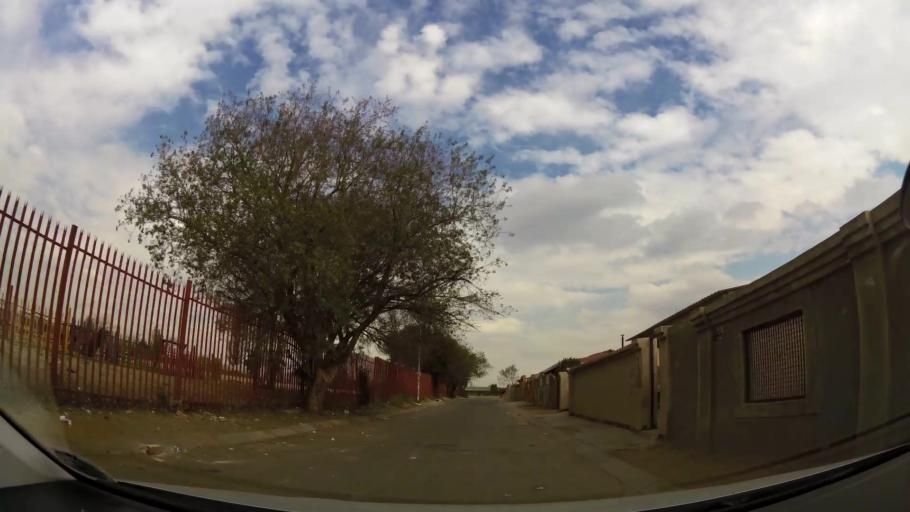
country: ZA
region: Gauteng
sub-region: City of Johannesburg Metropolitan Municipality
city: Soweto
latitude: -26.2719
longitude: 27.8623
